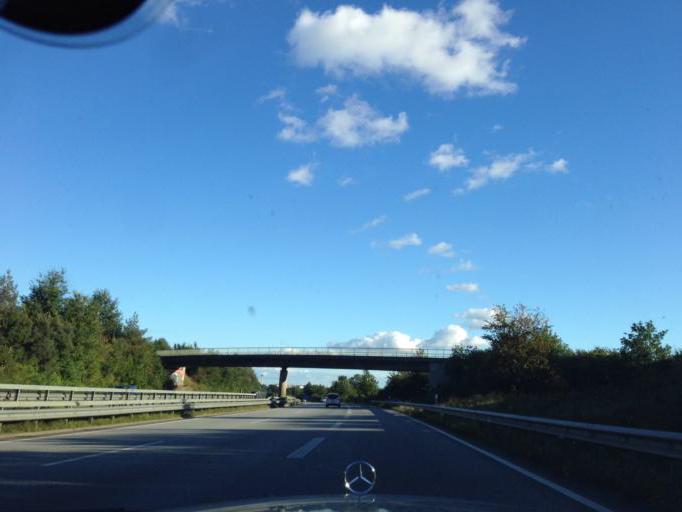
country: DE
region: Schleswig-Holstein
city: Schackendorf
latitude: 53.9579
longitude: 10.2635
